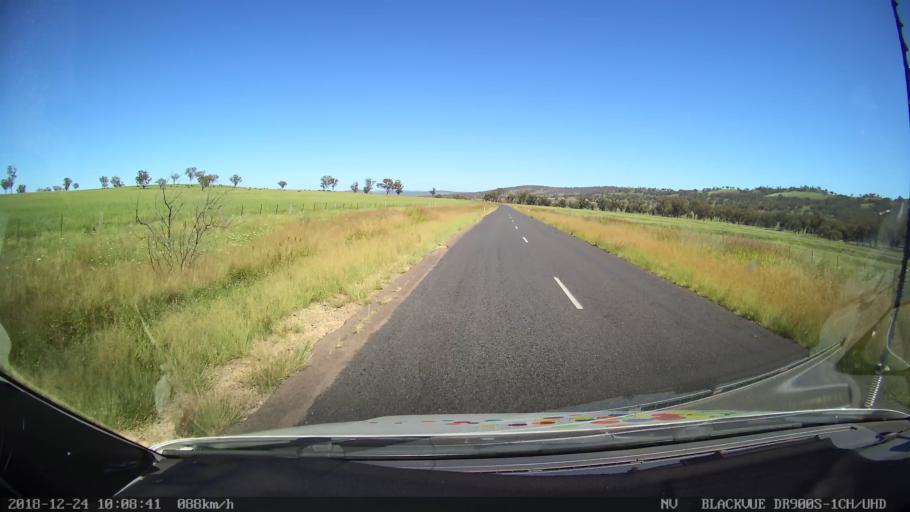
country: AU
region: New South Wales
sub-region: Liverpool Plains
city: Quirindi
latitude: -31.6661
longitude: 150.7012
